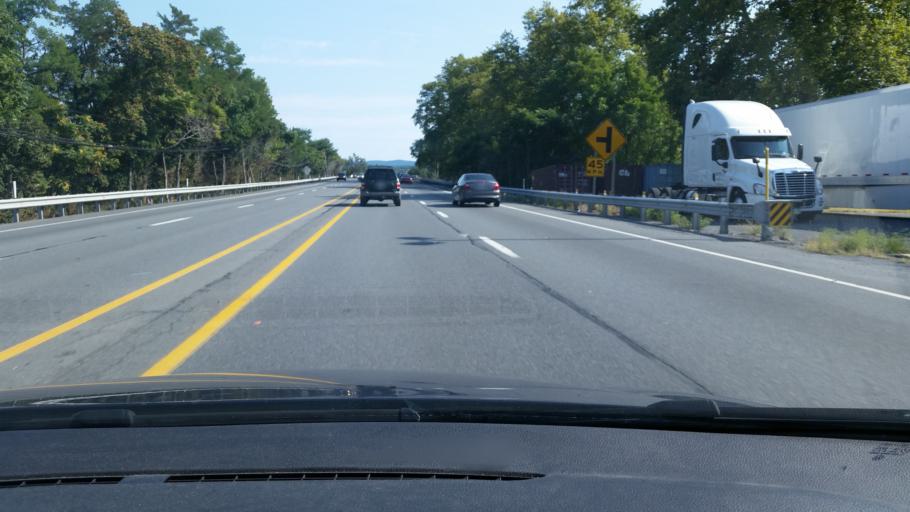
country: US
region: Pennsylvania
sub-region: Berks County
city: Shoemakersville
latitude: 40.5256
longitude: -75.9739
